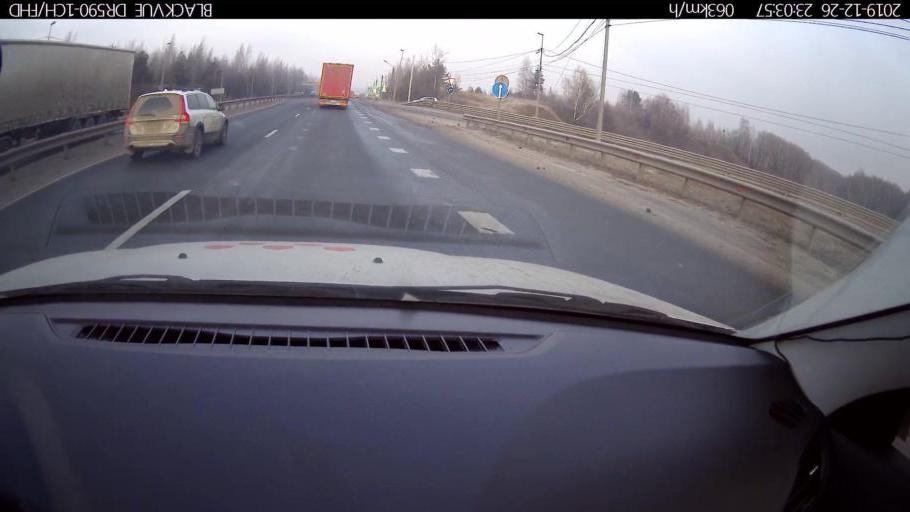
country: RU
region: Nizjnij Novgorod
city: Burevestnik
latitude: 56.1739
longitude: 43.7481
